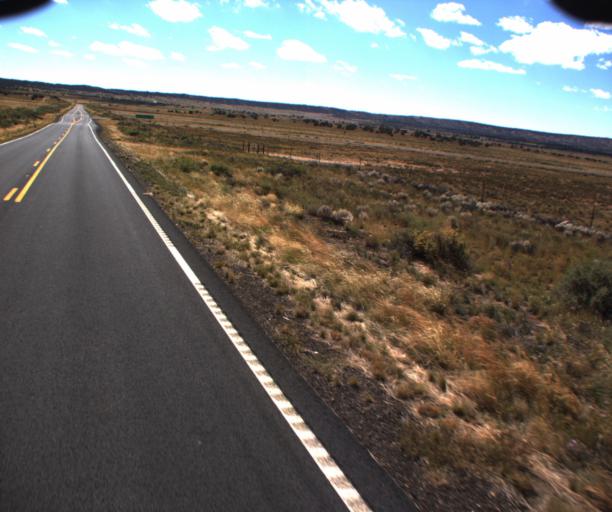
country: US
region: Arizona
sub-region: Apache County
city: Houck
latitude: 35.0658
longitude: -109.2837
